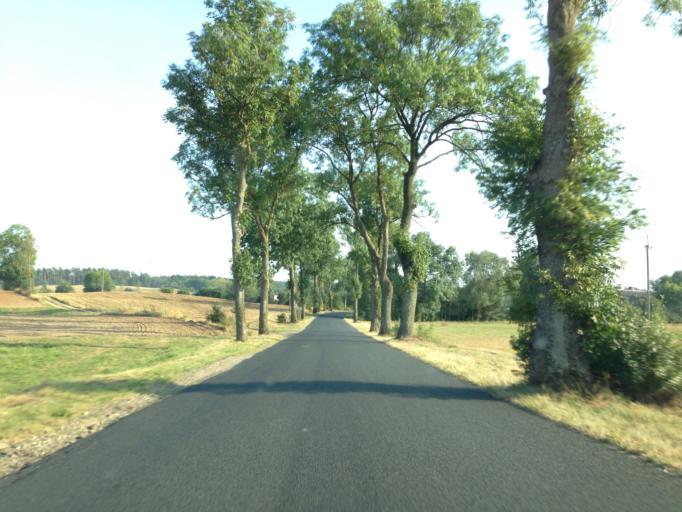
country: PL
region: Kujawsko-Pomorskie
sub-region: Powiat brodnicki
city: Brodnica
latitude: 53.3733
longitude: 19.3737
